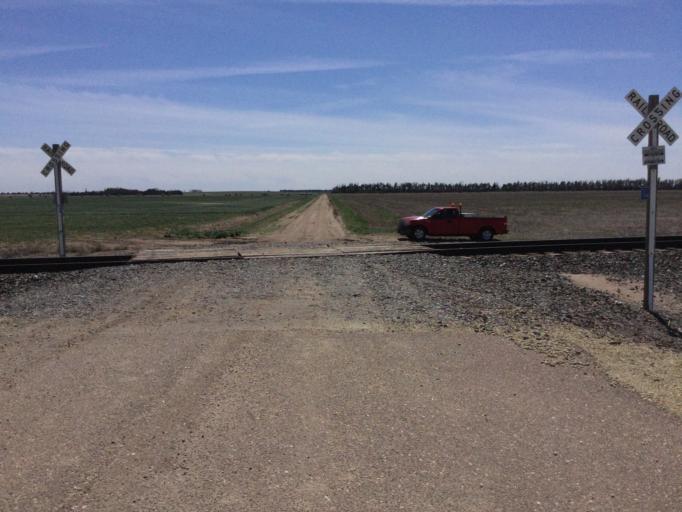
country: US
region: Kansas
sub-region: Edwards County
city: Kinsley
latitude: 37.8954
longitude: -99.5328
